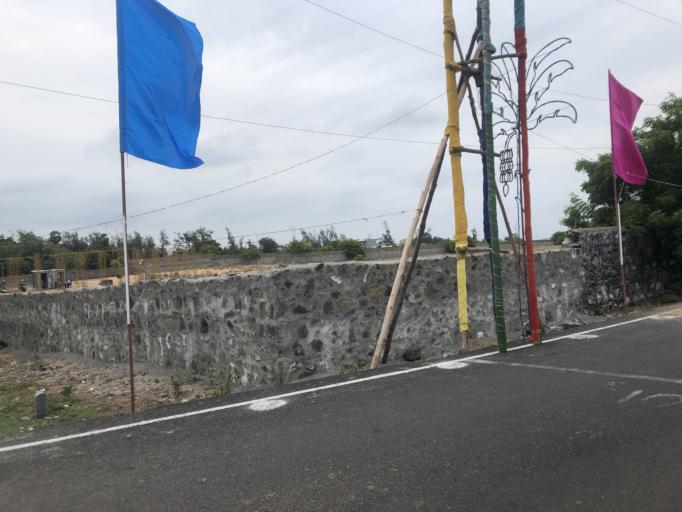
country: IN
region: Tamil Nadu
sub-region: Kancheepuram
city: Mamallapuram
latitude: 12.5996
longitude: 80.1873
